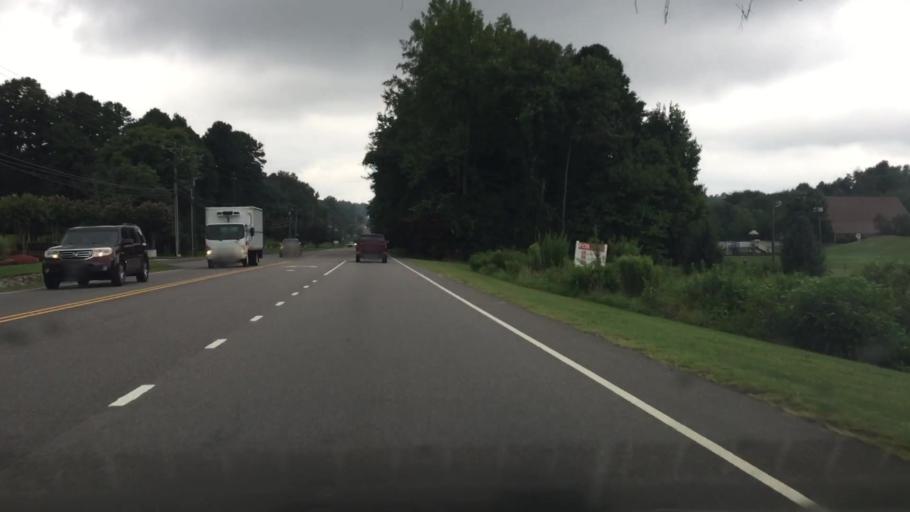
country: US
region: North Carolina
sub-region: Iredell County
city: Mooresville
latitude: 35.5744
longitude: -80.8429
